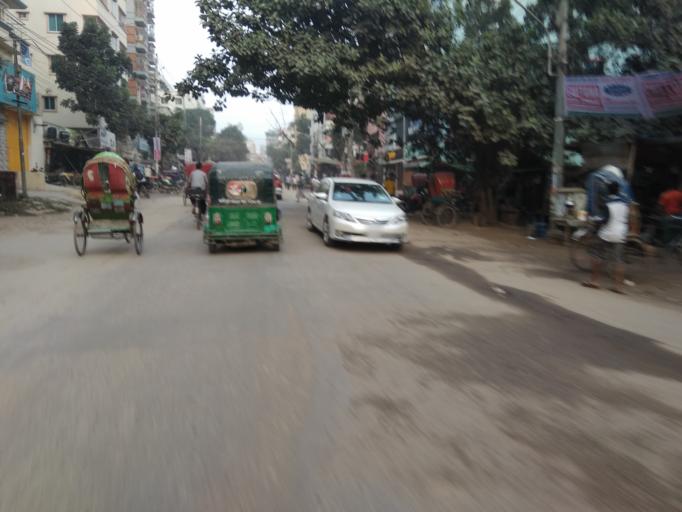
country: BD
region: Dhaka
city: Tungi
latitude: 23.8175
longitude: 90.3587
